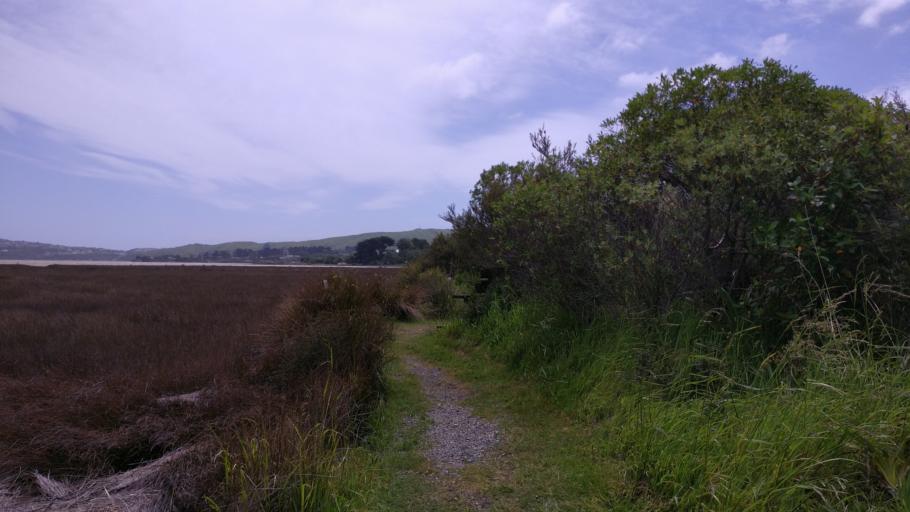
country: NZ
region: Wellington
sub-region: Porirua City
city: Porirua
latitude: -41.1017
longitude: 174.9150
